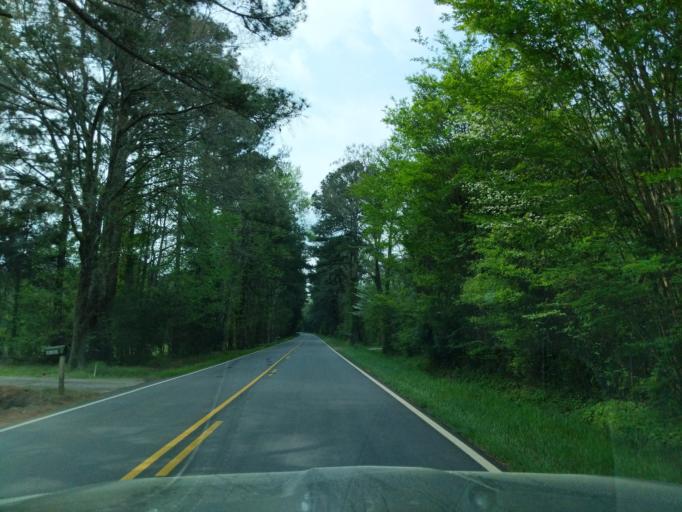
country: US
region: Georgia
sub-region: Columbia County
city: Appling
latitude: 33.6371
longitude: -82.3407
